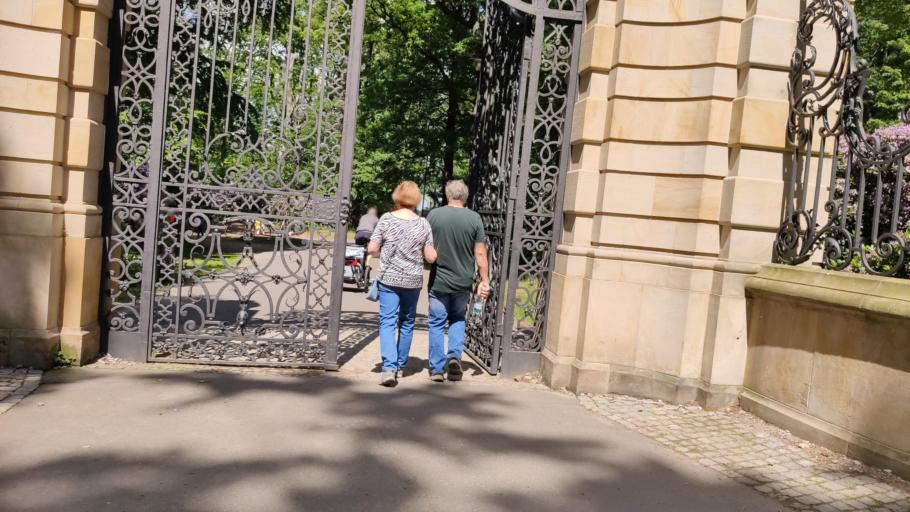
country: PL
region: Lower Silesian Voivodeship
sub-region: Powiat swidnicki
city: Swiebodzice
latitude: 50.8392
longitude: 16.2991
